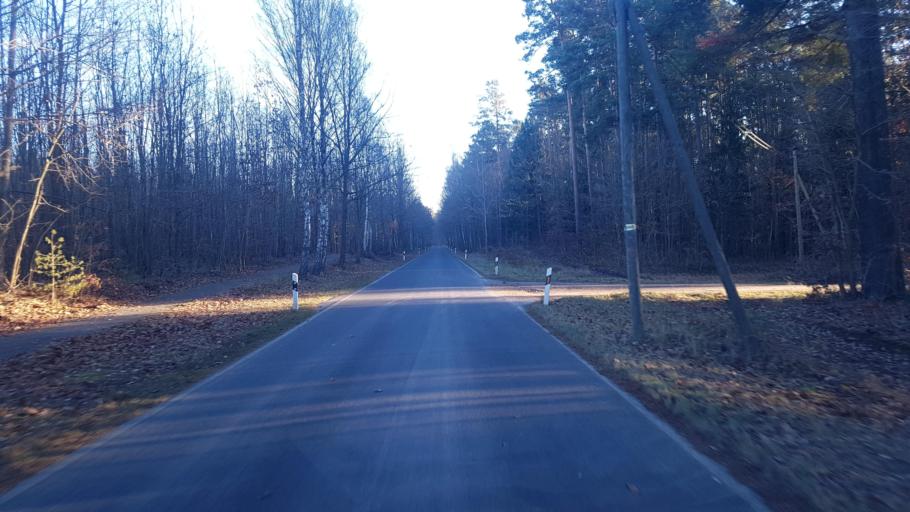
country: DE
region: Brandenburg
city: Tauer
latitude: 51.9319
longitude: 14.4828
